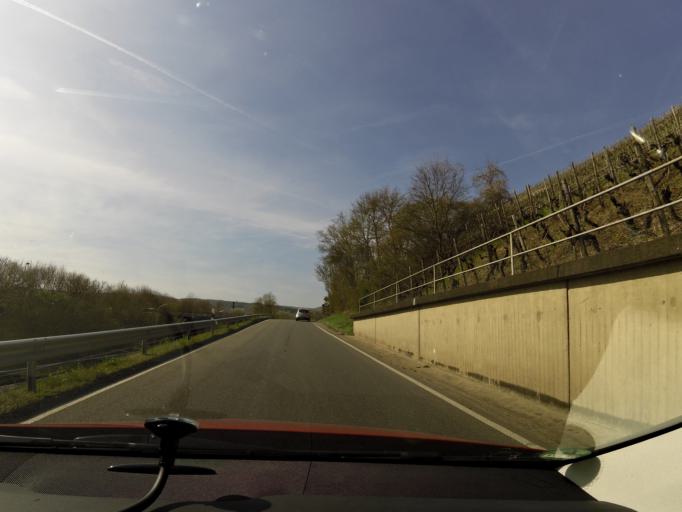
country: DE
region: Rheinland-Pfalz
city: Konigsfeld
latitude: 50.5485
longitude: 7.1834
